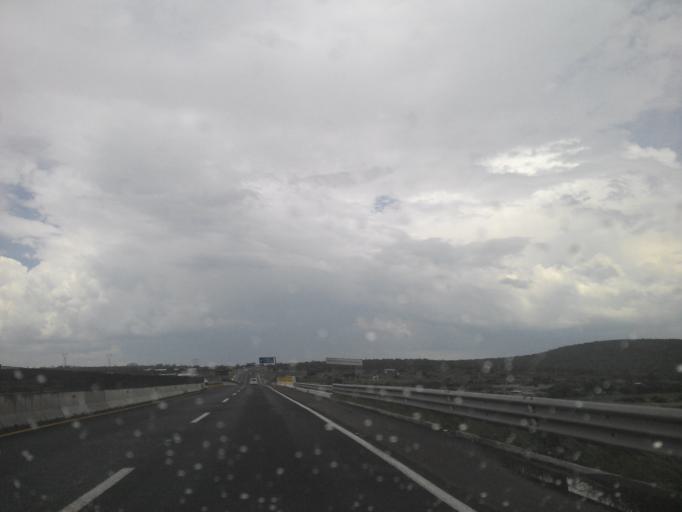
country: MX
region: Hidalgo
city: Tula de Allende
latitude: 20.0687
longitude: -99.3746
